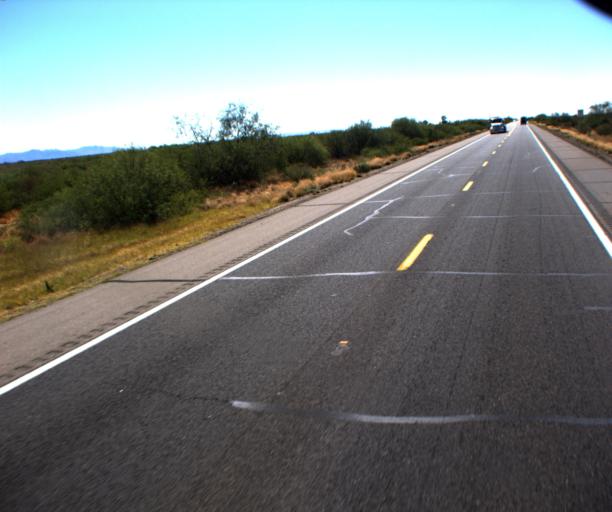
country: US
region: Arizona
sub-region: Yavapai County
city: Congress
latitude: 34.1563
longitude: -112.9979
